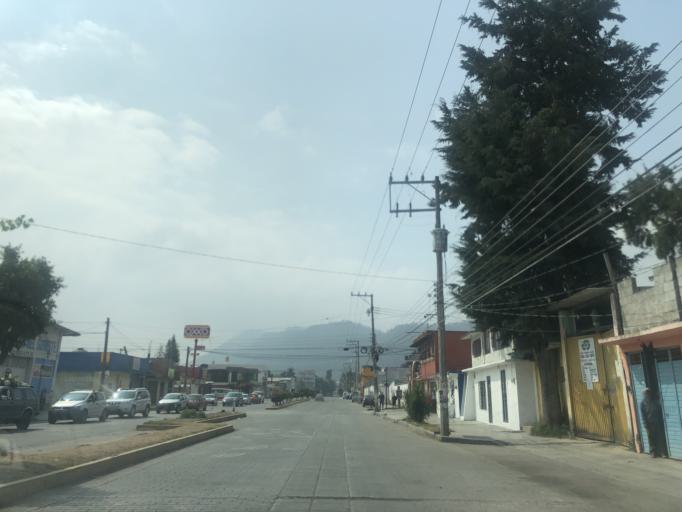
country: MX
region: Chiapas
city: San Cristobal de las Casas
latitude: 16.7165
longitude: -92.6363
